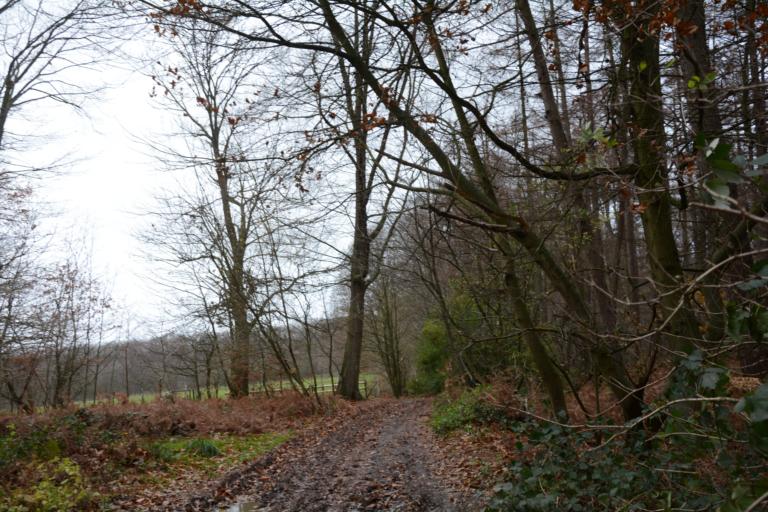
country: BE
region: Flanders
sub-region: Provincie Vlaams-Brabant
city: Opwijk
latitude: 50.9339
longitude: 4.1603
